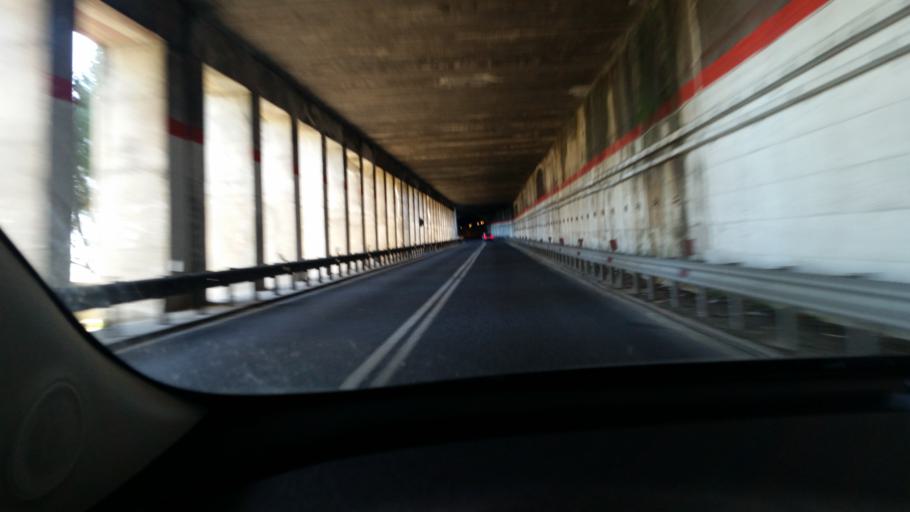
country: IT
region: Calabria
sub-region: Provincia di Catanzaro
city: Squillace Lido
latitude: 38.7659
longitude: 16.5640
